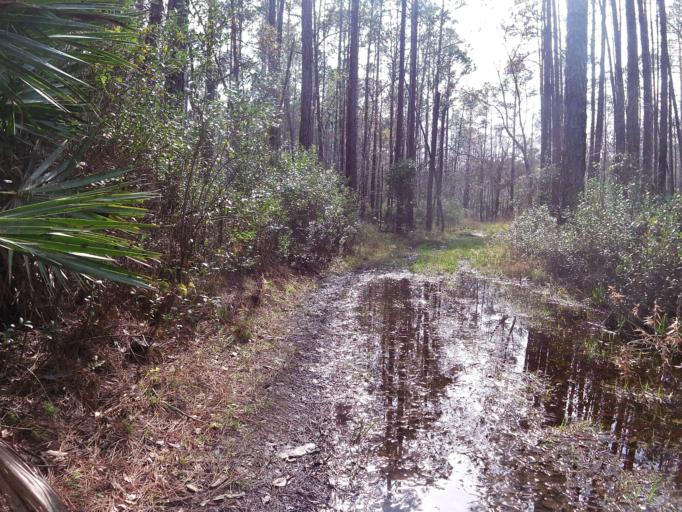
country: US
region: Florida
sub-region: Clay County
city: Middleburg
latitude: 30.1255
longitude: -81.9084
